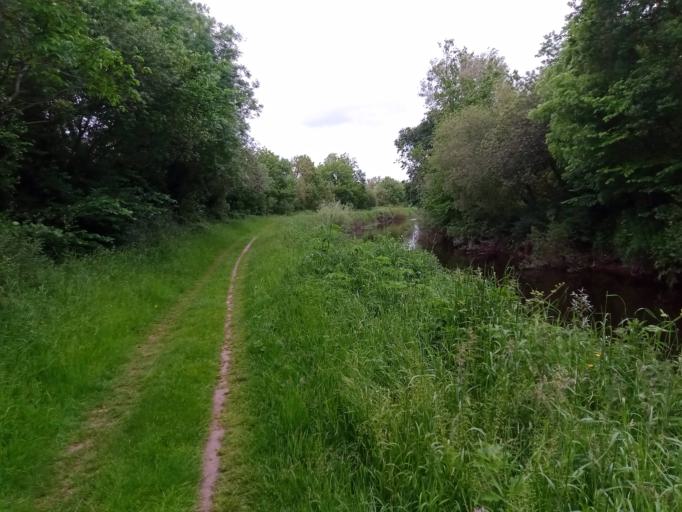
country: IE
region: Leinster
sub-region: County Carlow
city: Carlow
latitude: 52.8190
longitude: -6.9501
